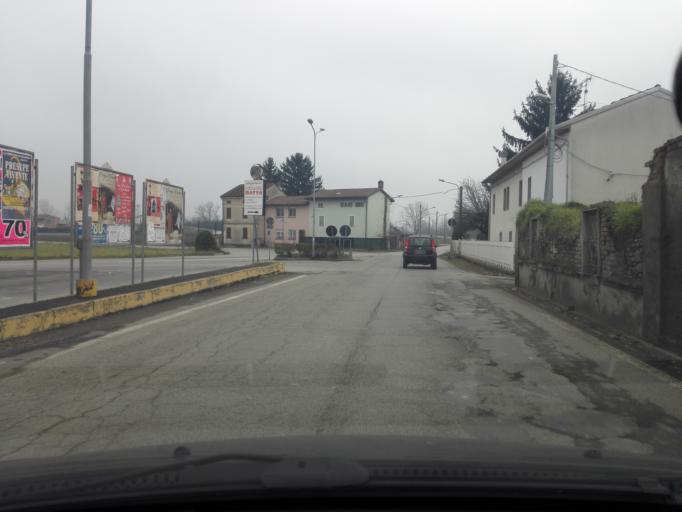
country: IT
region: Piedmont
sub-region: Provincia di Alessandria
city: Casal Cermelli
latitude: 44.8351
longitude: 8.6267
